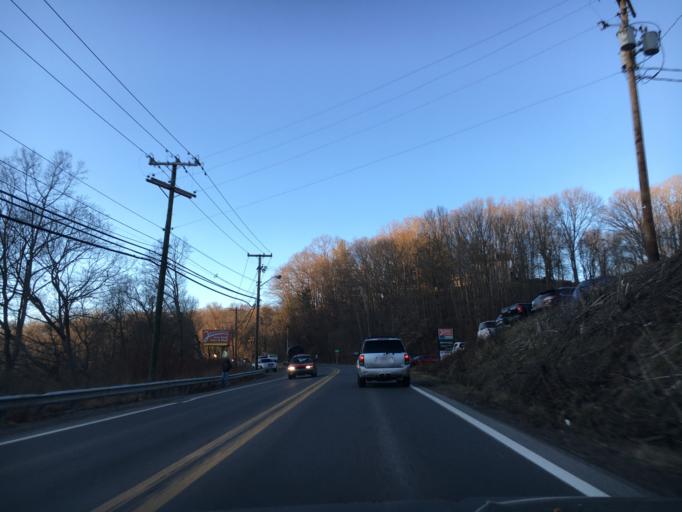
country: US
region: West Virginia
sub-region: Raleigh County
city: Beaver
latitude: 37.7591
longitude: -81.1580
